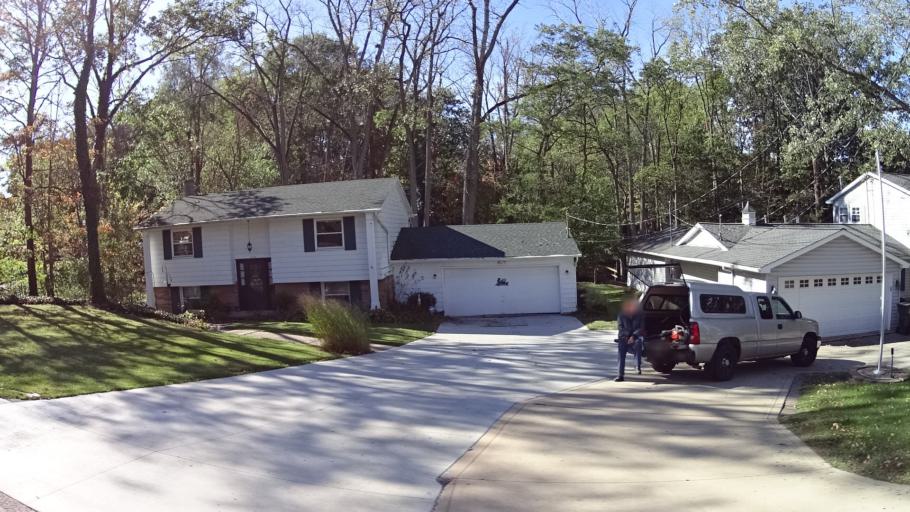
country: US
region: Ohio
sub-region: Lorain County
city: Amherst
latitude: 41.3904
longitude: -82.2397
